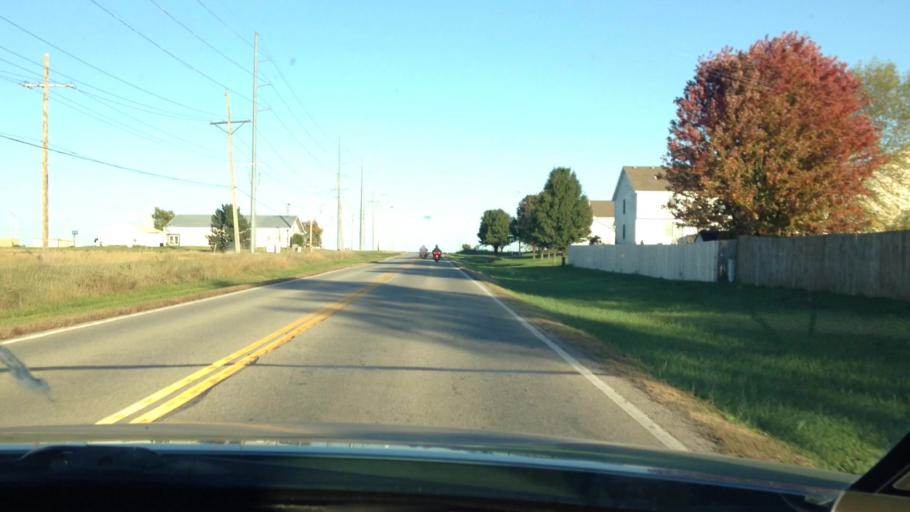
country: US
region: Kansas
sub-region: Johnson County
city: Gardner
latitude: 38.8255
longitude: -94.9125
